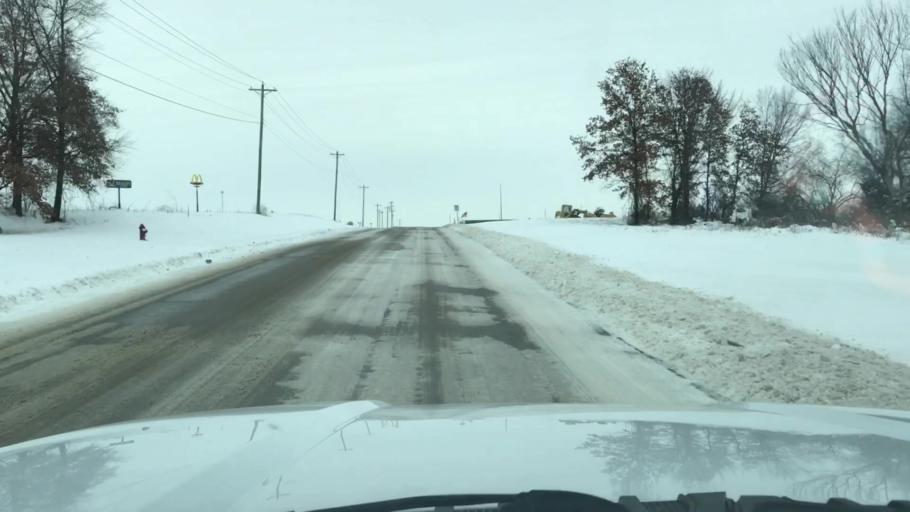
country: US
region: Missouri
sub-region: Clinton County
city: Cameron
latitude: 39.7487
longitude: -94.2153
